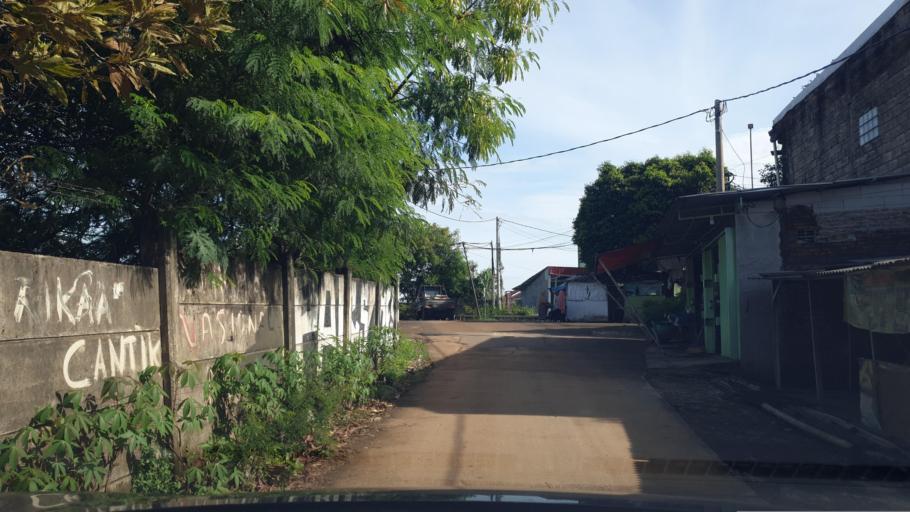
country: ID
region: West Java
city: Sawangan
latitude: -6.3778
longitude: 106.7876
